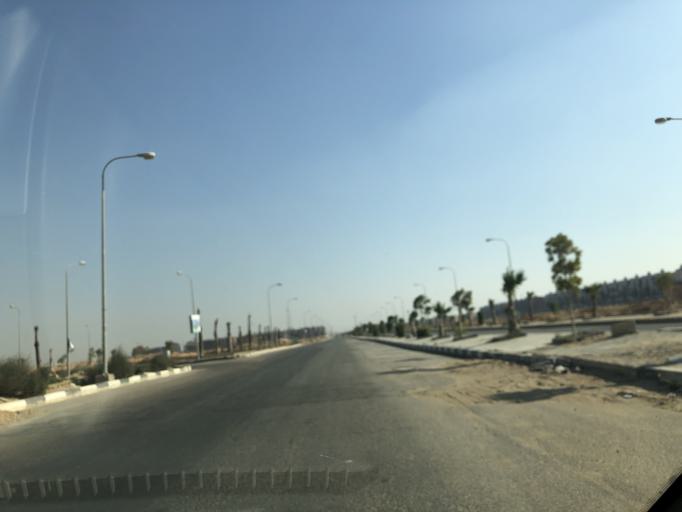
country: EG
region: Al Jizah
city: Madinat Sittah Uktubar
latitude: 29.9134
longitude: 31.0683
